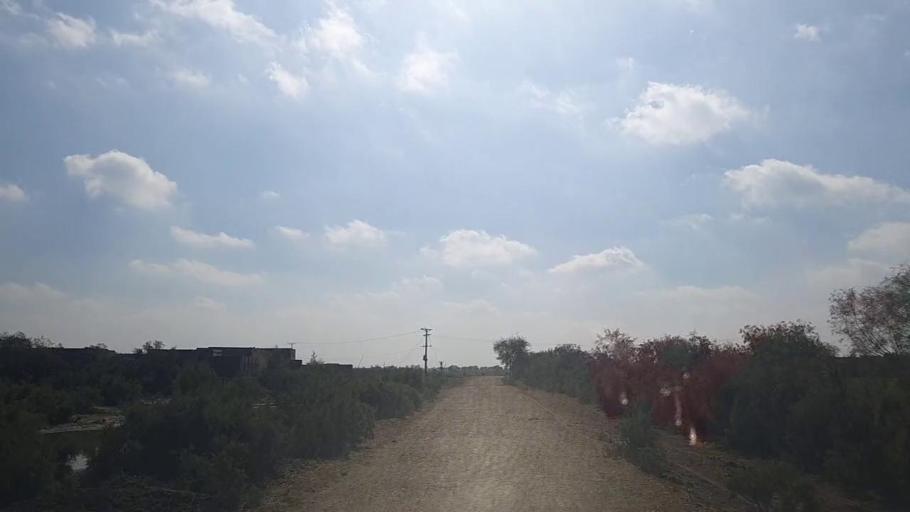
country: PK
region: Sindh
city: Sanghar
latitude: 26.0482
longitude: 69.0045
